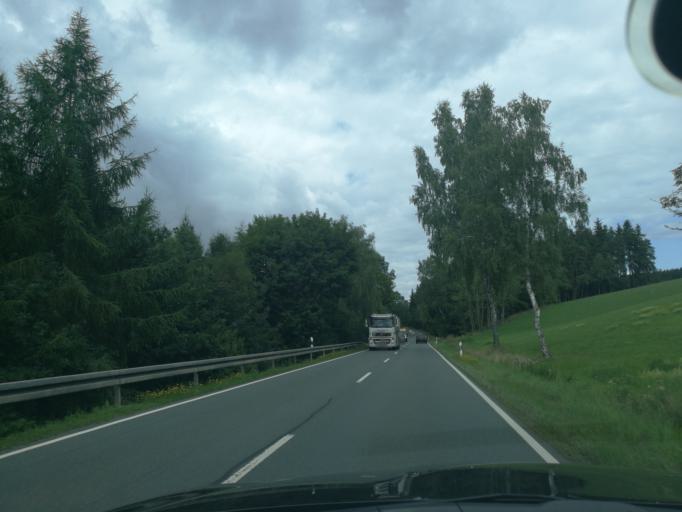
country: DE
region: Saxony
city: Adorf
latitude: 50.3575
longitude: 12.2263
